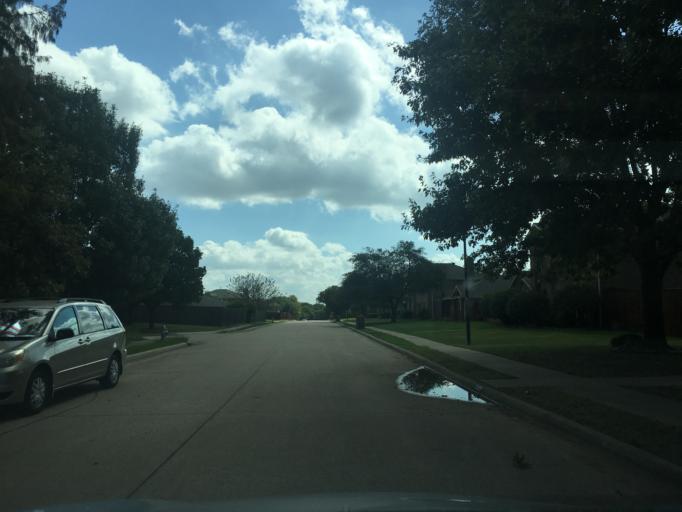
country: US
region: Texas
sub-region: Dallas County
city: Sachse
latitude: 32.9703
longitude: -96.5982
